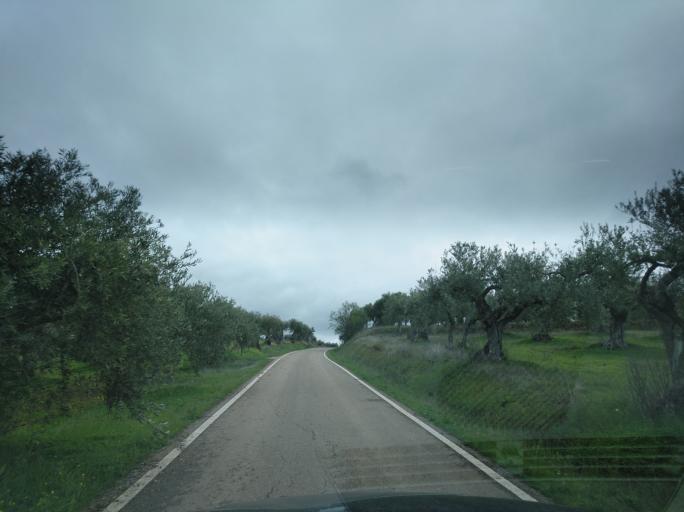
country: PT
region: Portalegre
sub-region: Campo Maior
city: Campo Maior
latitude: 38.9872
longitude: -7.0423
